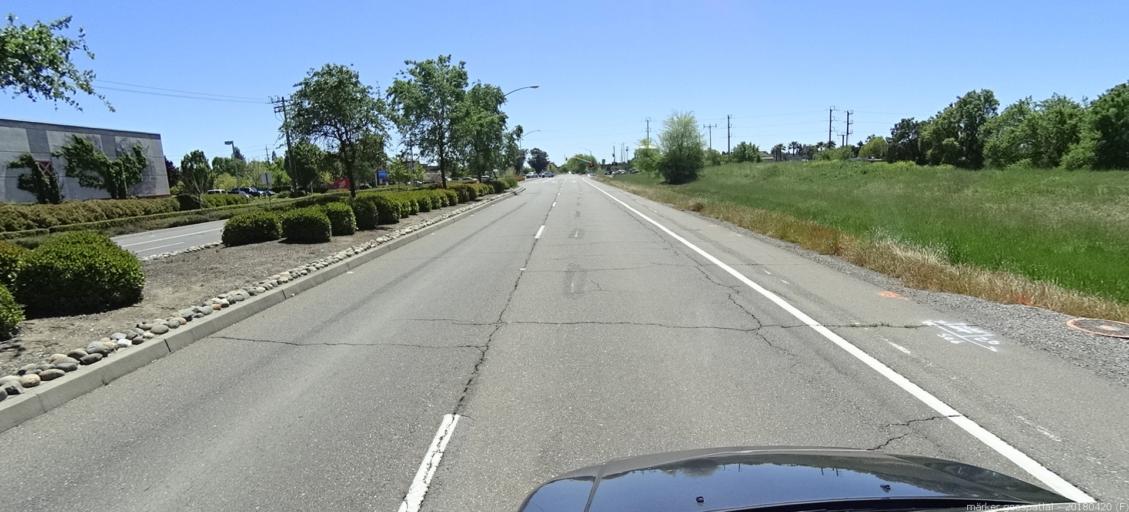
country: US
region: California
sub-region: Sacramento County
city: Parkway
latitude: 38.4831
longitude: -121.5055
